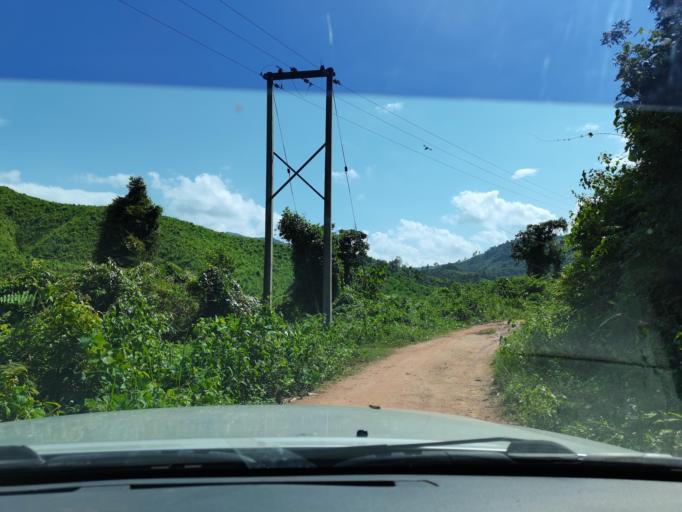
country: LA
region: Loungnamtha
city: Muang Nale
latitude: 20.5563
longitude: 101.0611
